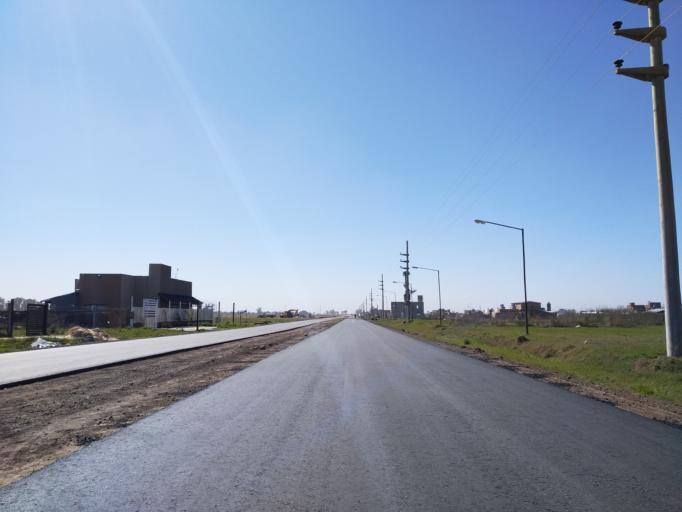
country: AR
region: Santa Fe
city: Funes
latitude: -32.8990
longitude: -60.8161
